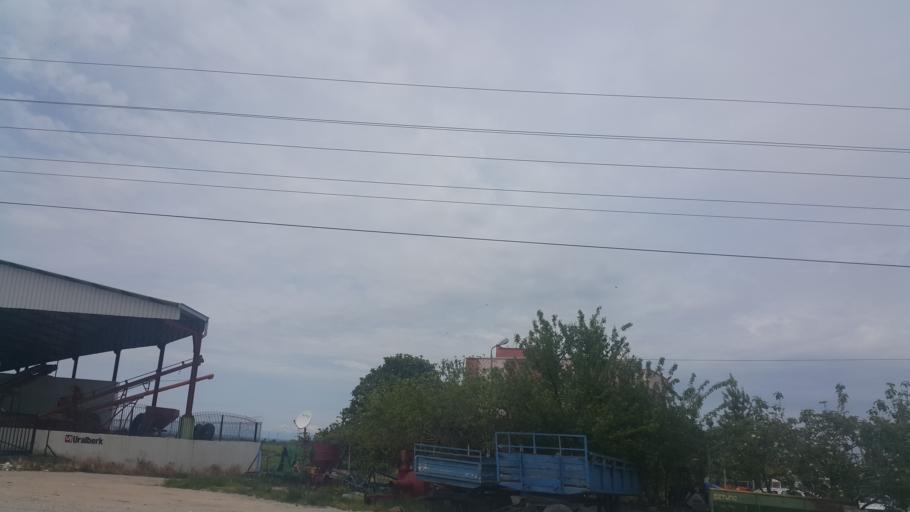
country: TR
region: Adana
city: Ceyhan
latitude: 37.0447
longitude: 35.7637
